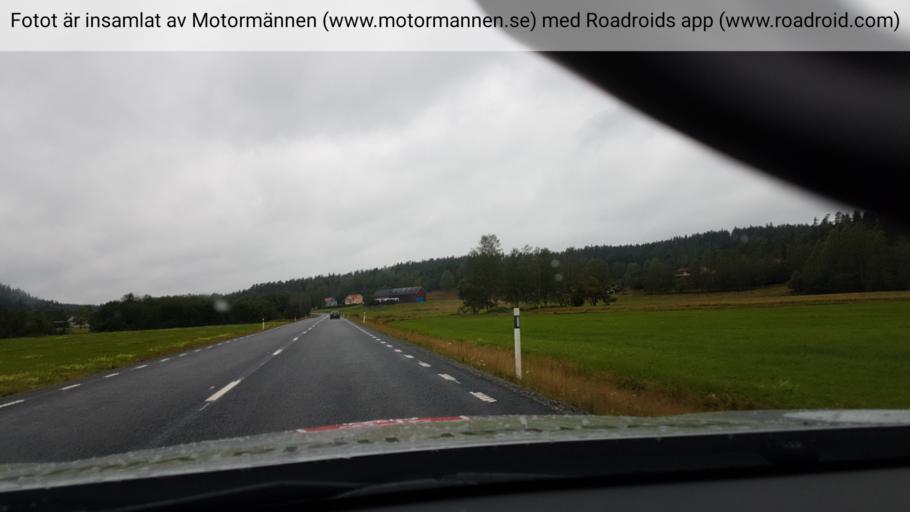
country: SE
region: Vaestra Goetaland
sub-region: Dals-Ed Kommun
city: Ed
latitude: 58.9137
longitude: 12.0153
